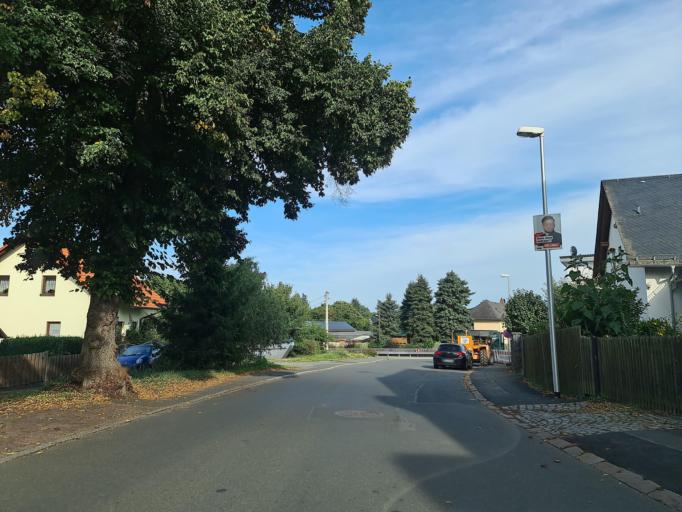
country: DE
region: Saxony
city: Plauen
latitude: 50.4893
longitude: 12.0981
